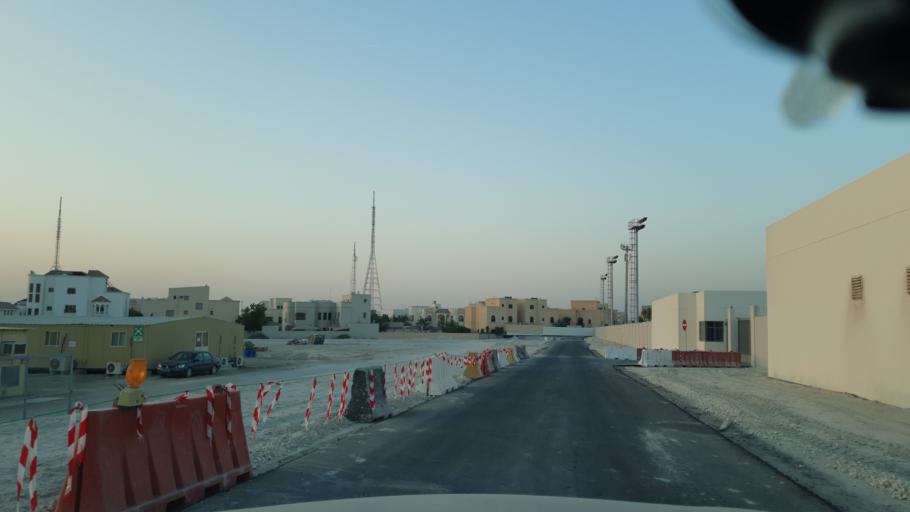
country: BH
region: Northern
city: Madinat `Isa
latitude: 26.1555
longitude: 50.5598
